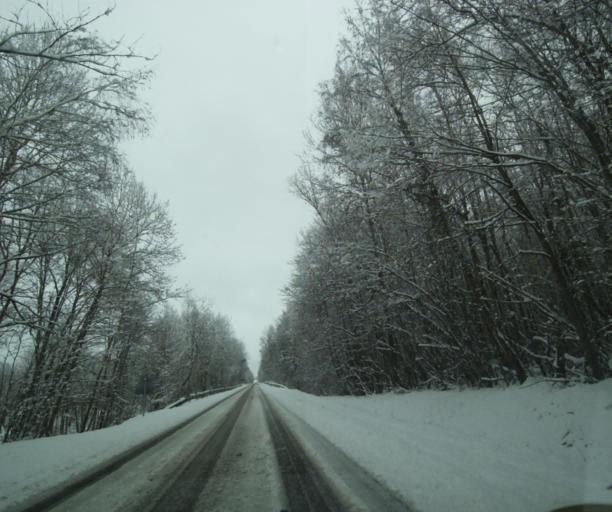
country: FR
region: Champagne-Ardenne
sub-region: Departement de la Haute-Marne
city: Montier-en-Der
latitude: 48.5298
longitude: 4.7892
